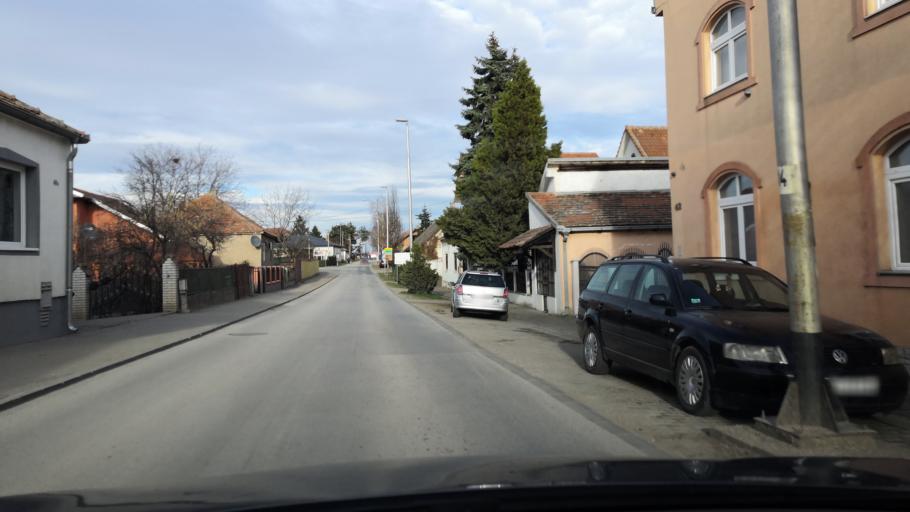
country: RS
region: Autonomna Pokrajina Vojvodina
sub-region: Sremski Okrug
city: Ingija
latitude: 45.0438
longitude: 20.0931
